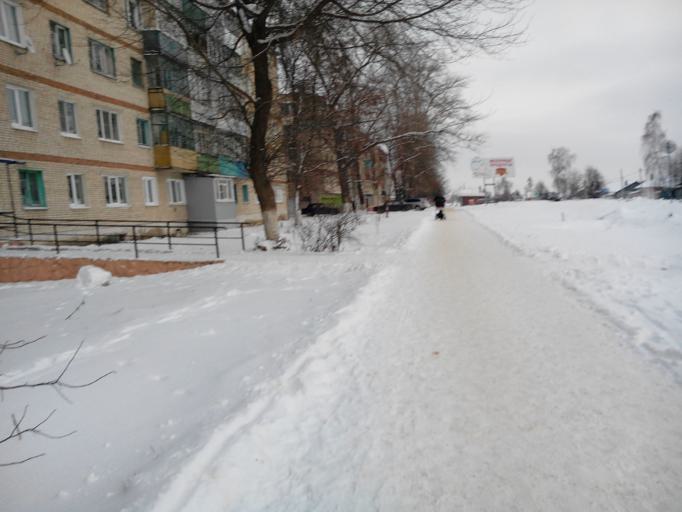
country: RU
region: Tula
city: Yefremov
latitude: 53.1486
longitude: 38.0817
